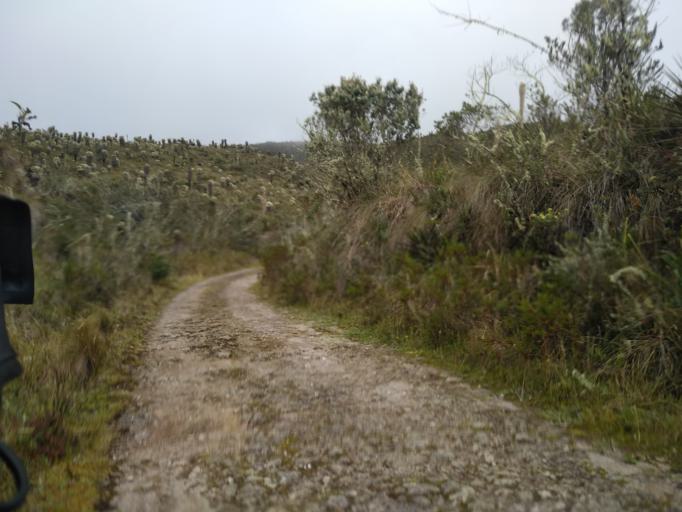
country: EC
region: Carchi
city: San Gabriel
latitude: 0.6948
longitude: -77.8457
